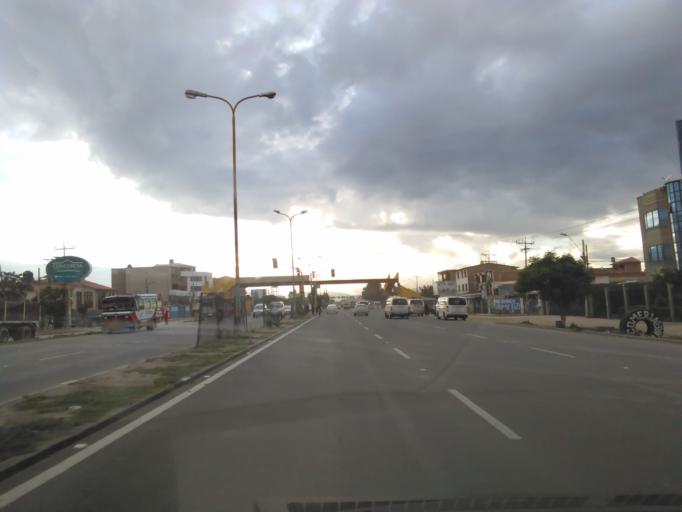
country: BO
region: Cochabamba
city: Cochabamba
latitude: -17.3916
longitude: -66.2229
